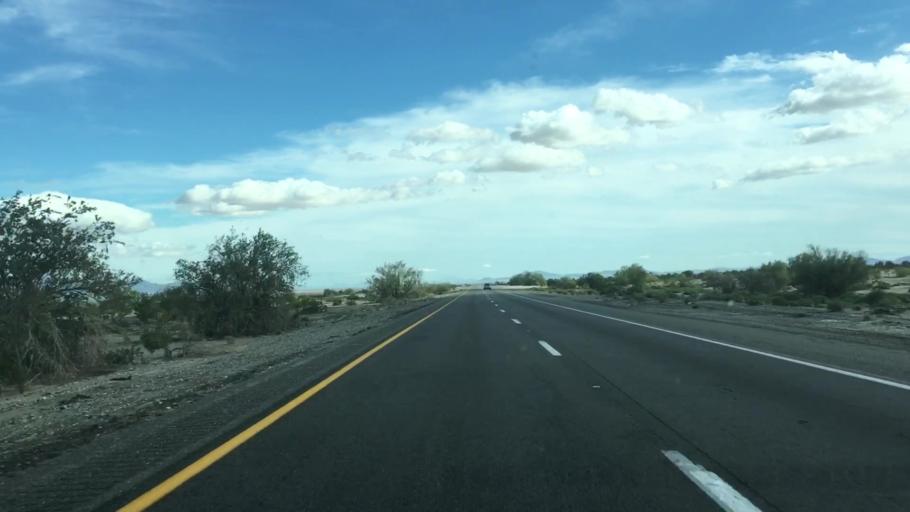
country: US
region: California
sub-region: Riverside County
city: Mesa Verde
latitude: 33.6590
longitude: -115.1646
